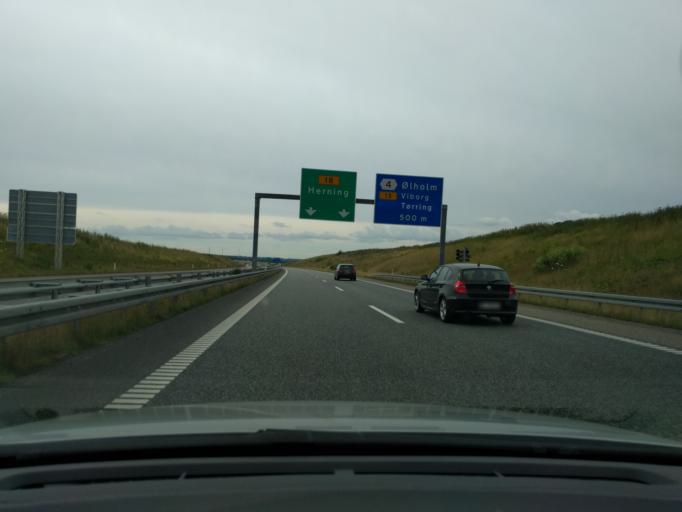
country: DK
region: Central Jutland
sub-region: Hedensted Kommune
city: Torring
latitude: 55.8267
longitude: 9.5308
